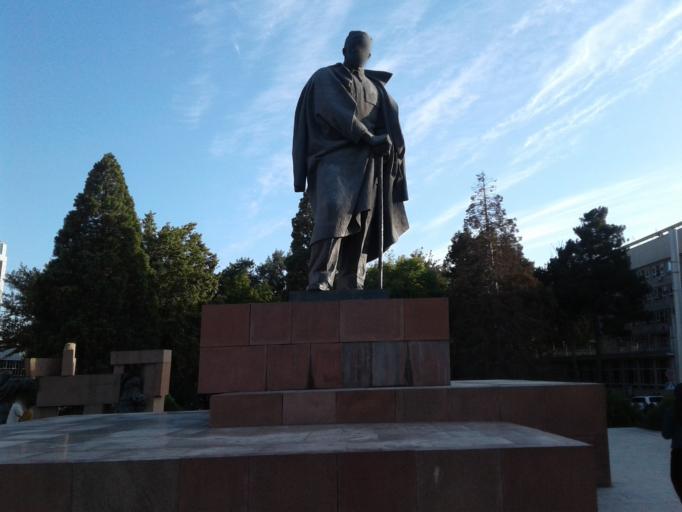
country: TJ
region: Dushanbe
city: Dushanbe
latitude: 38.5626
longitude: 68.7992
